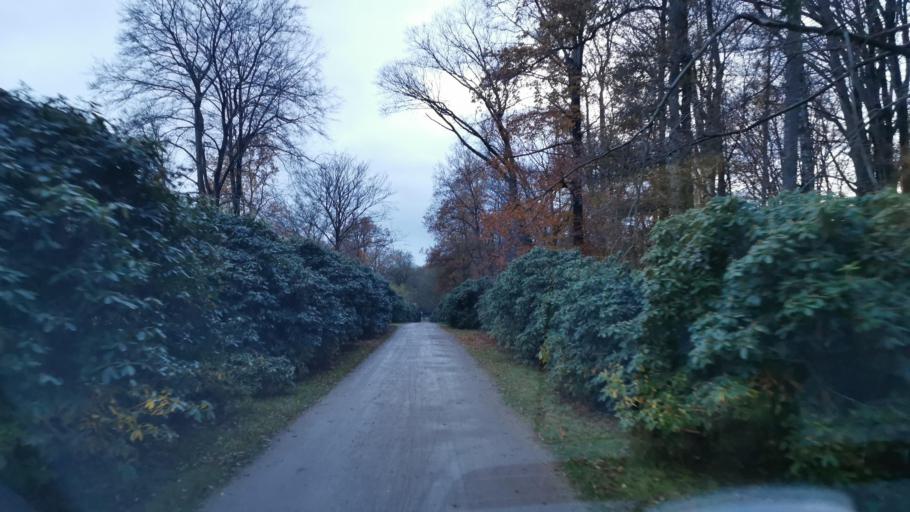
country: NL
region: Overijssel
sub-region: Gemeente Oldenzaal
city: Oldenzaal
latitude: 52.3129
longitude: 6.9520
